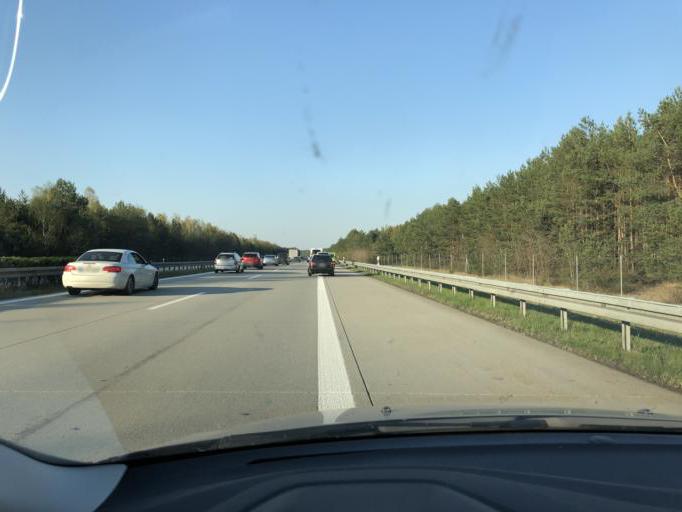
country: DE
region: Brandenburg
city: Ruhland
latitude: 51.4333
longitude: 13.8259
